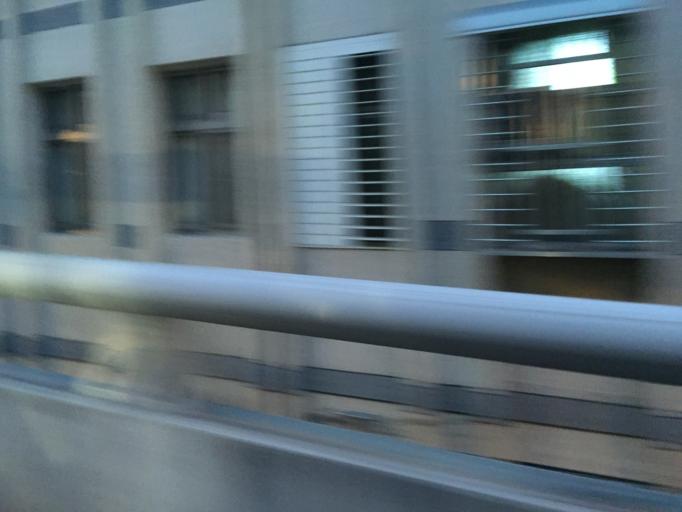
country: TW
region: Taiwan
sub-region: Yilan
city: Yilan
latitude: 24.7572
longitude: 121.7457
